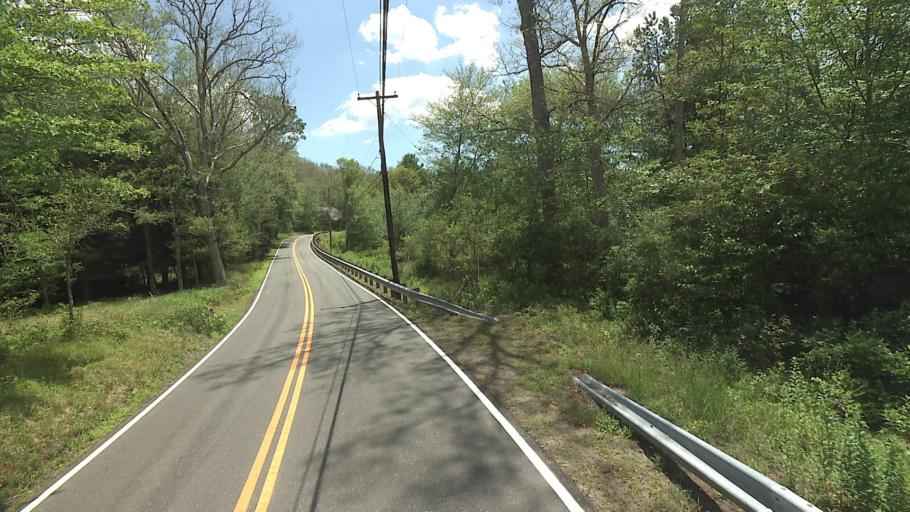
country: US
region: Connecticut
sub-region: New London County
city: Colchester
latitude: 41.4901
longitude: -72.3451
